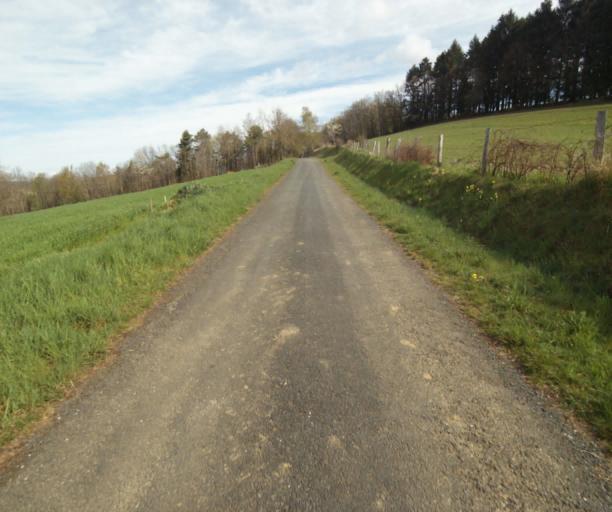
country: FR
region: Limousin
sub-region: Departement de la Correze
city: Laguenne
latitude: 45.2547
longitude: 1.8076
